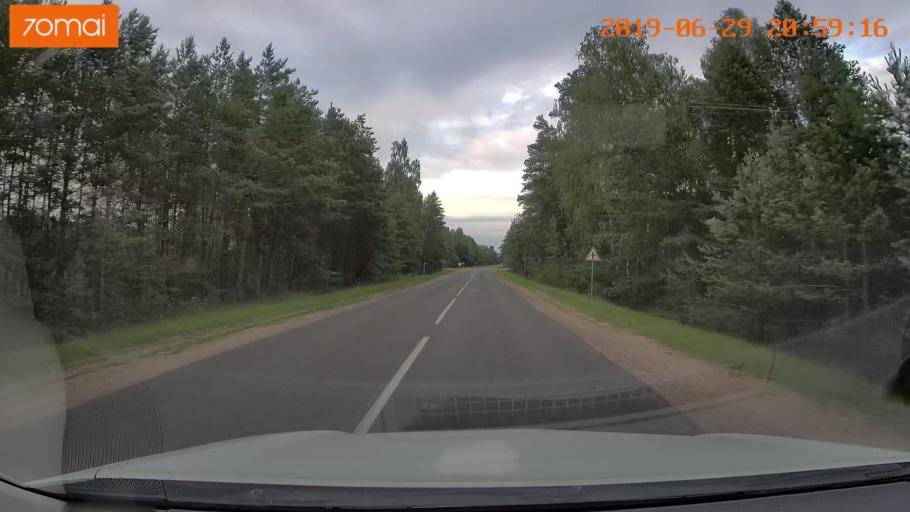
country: BY
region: Brest
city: Hantsavichy
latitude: 52.7362
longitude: 26.4029
